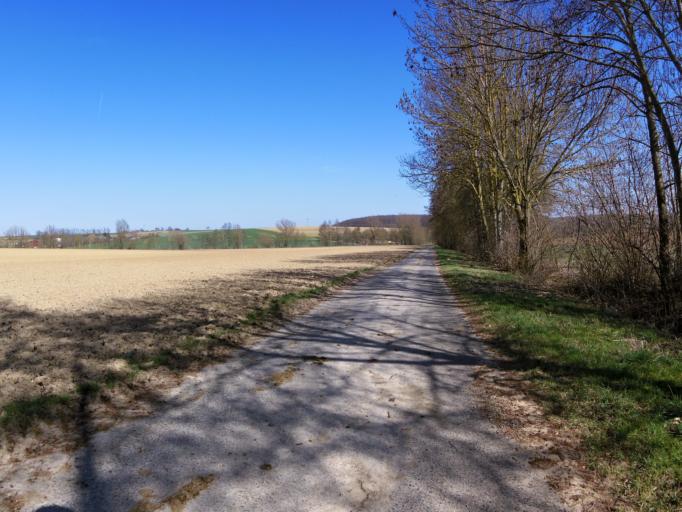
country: DE
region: Bavaria
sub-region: Regierungsbezirk Unterfranken
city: Prosselsheim
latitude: 49.8564
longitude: 10.1318
